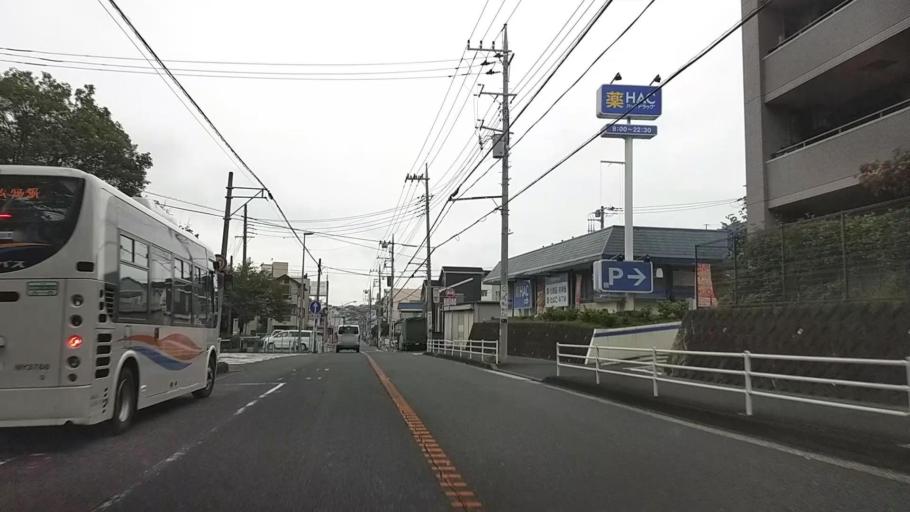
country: JP
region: Kanagawa
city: Yokohama
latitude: 35.4090
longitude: 139.6111
